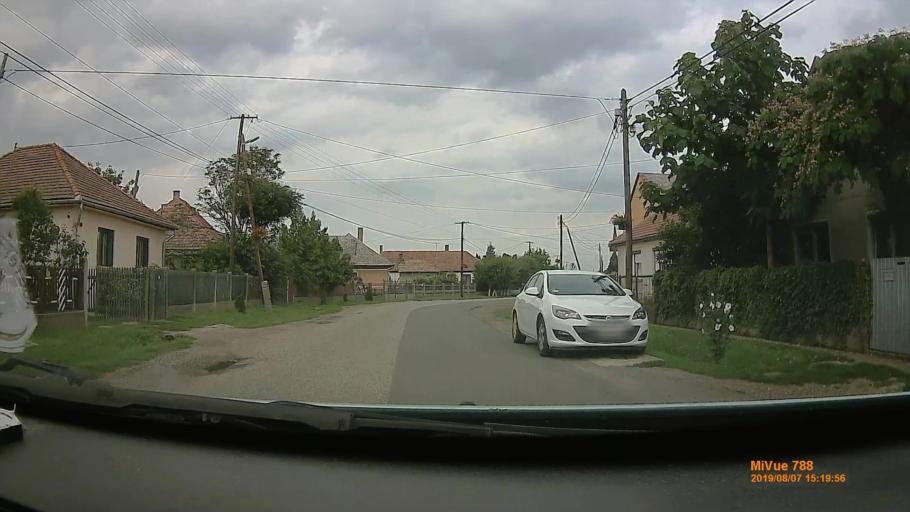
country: HU
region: Borsod-Abauj-Zemplen
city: Encs
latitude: 48.3528
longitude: 21.1448
